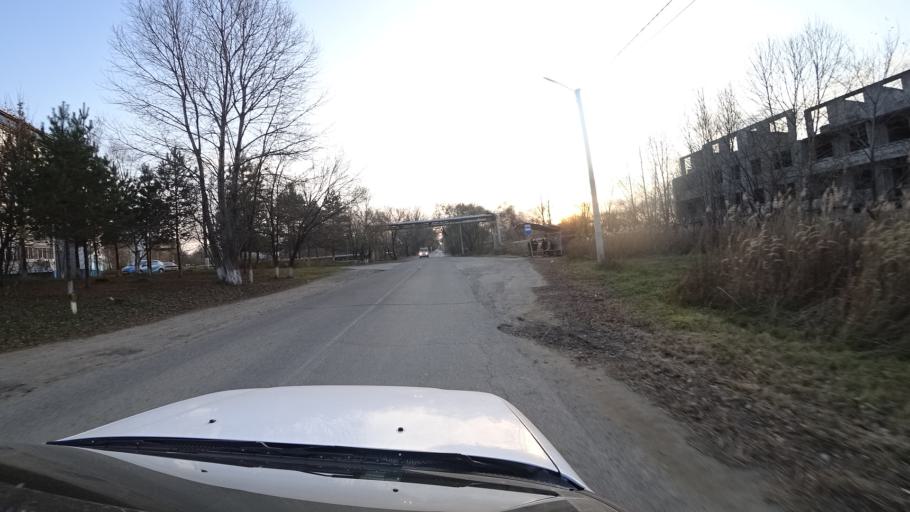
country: RU
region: Primorskiy
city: Dal'nerechensk
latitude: 45.9470
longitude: 133.8186
